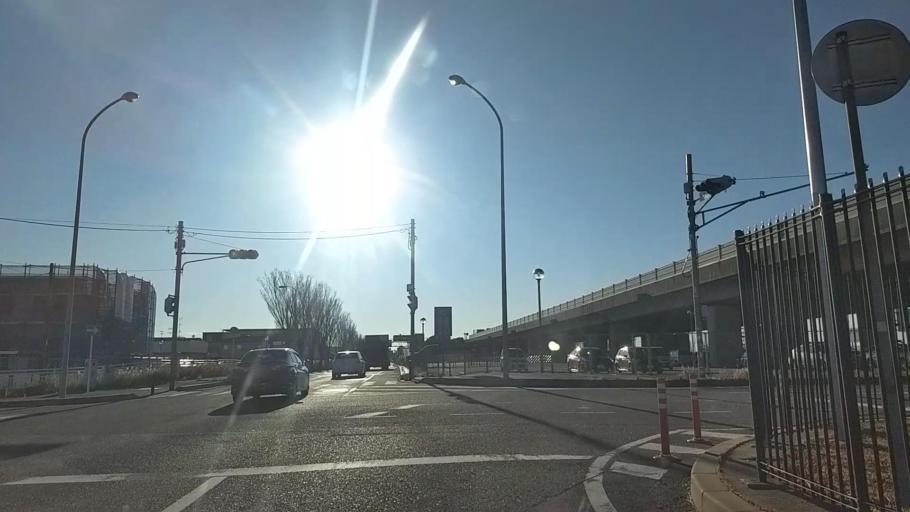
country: JP
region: Chiba
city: Kisarazu
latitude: 35.4320
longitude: 139.9246
